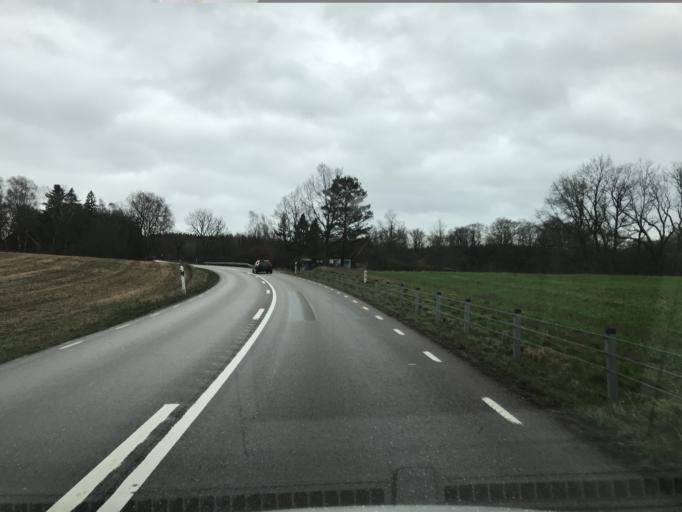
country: SE
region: Skane
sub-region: Klippans Kommun
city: Ljungbyhed
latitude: 56.1045
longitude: 13.1767
